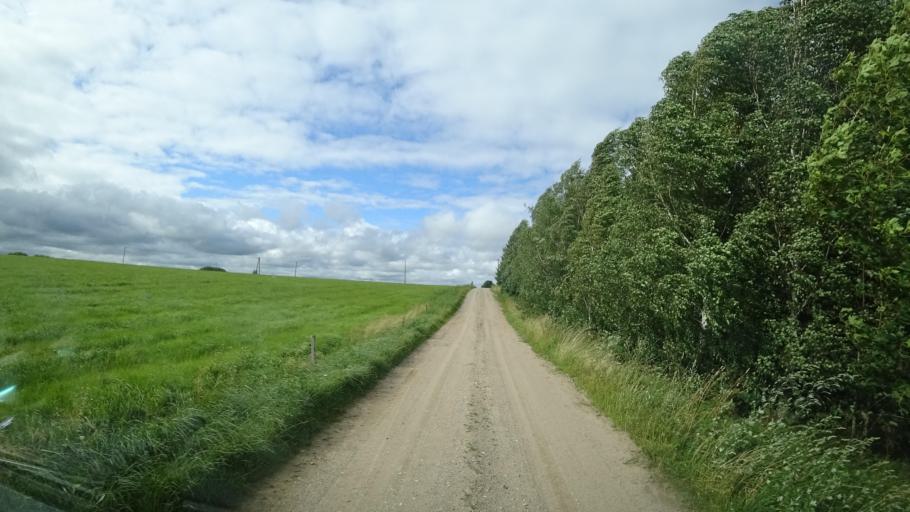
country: PL
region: Podlasie
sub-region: Suwalki
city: Suwalki
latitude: 54.3749
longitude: 22.9022
